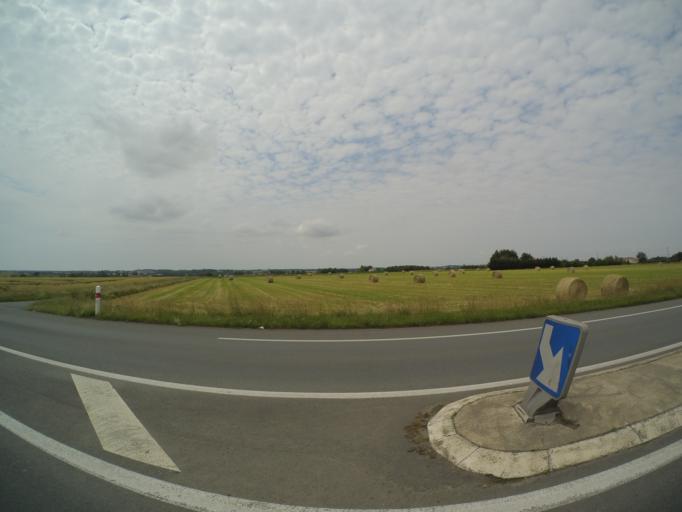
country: FR
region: Pays de la Loire
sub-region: Departement de la Vendee
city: Chavagnes-en-Paillers
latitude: 46.9125
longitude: -1.2403
